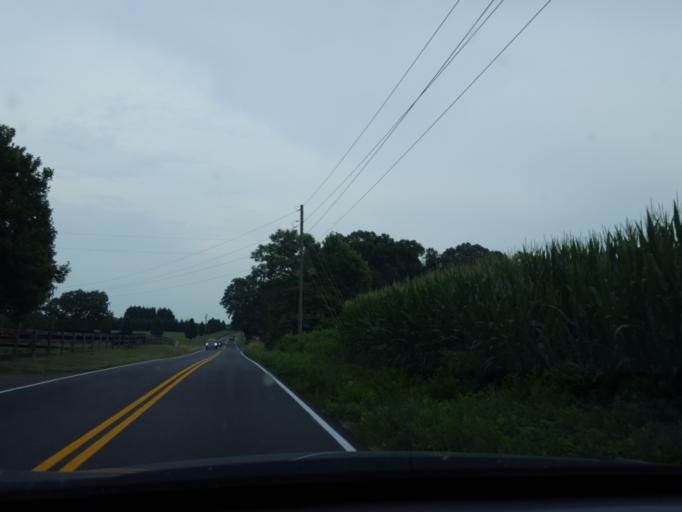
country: US
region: Virginia
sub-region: Spotsylvania County
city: Spotsylvania
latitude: 38.2666
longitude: -77.8071
